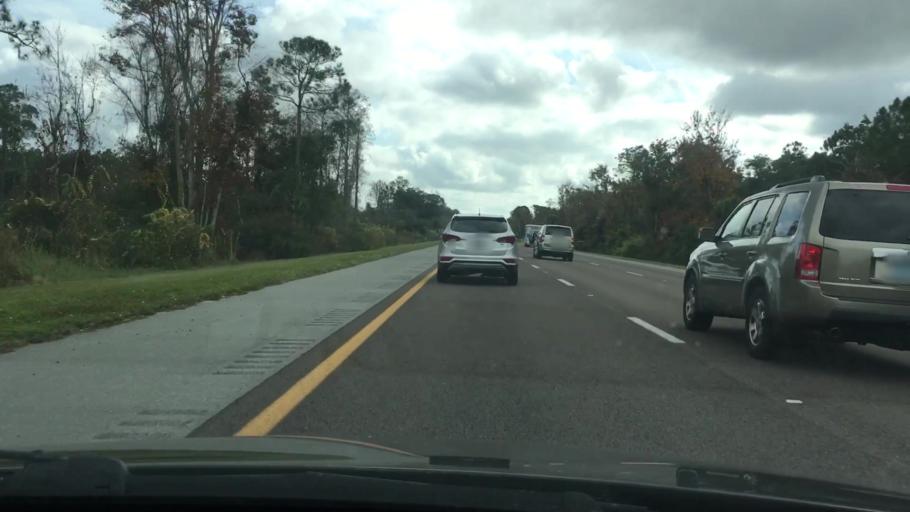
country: US
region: Florida
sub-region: Volusia County
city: Glencoe
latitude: 28.9764
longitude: -80.9644
